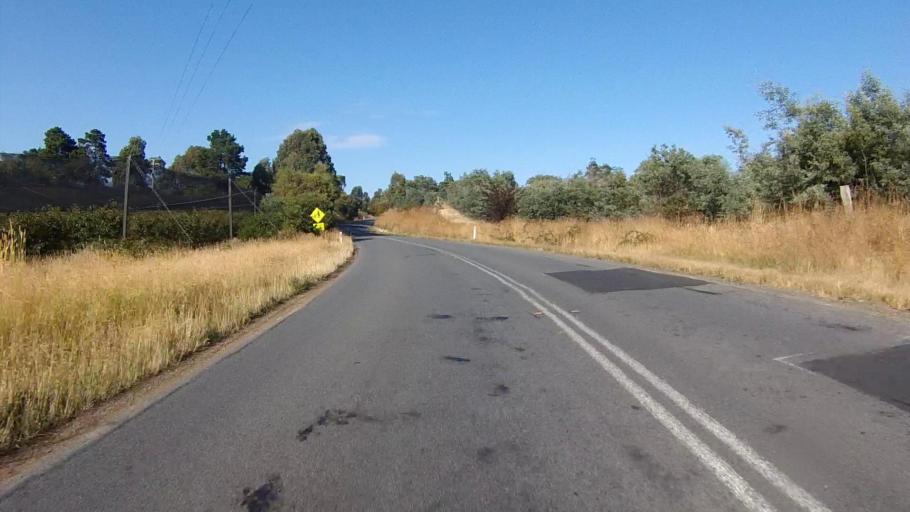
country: AU
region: Tasmania
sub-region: Derwent Valley
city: New Norfolk
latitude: -42.7620
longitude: 147.1341
